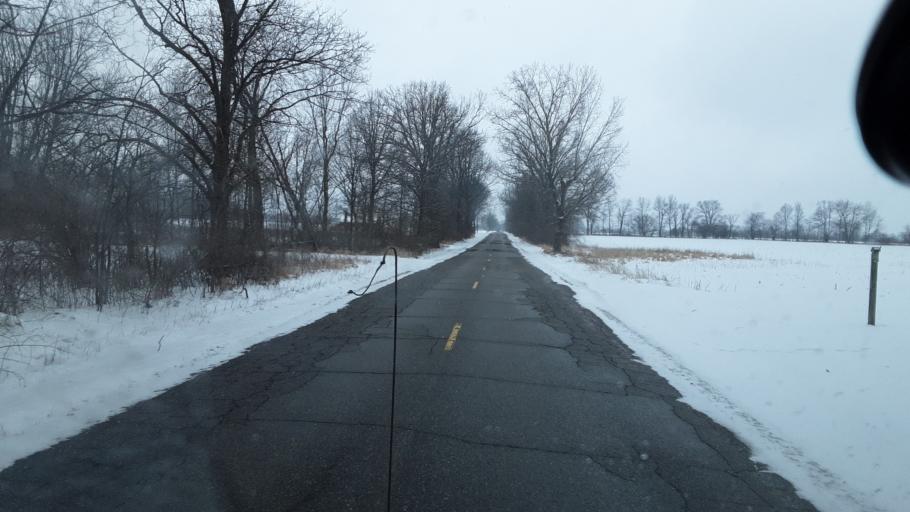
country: US
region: Michigan
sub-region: Ingham County
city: Leslie
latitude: 42.4755
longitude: -84.3941
